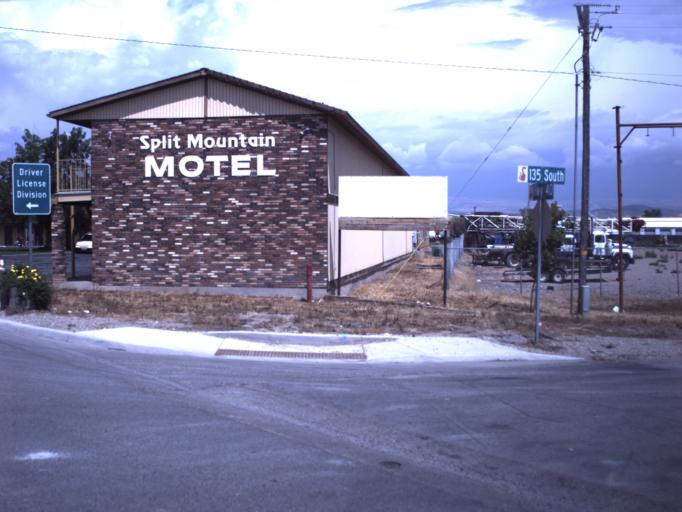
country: US
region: Utah
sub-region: Uintah County
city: Vernal
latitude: 40.4538
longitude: -109.5085
